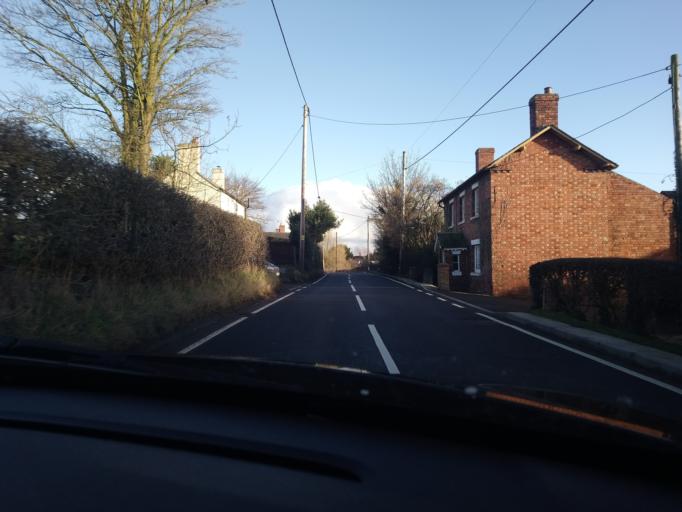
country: GB
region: England
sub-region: Shropshire
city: Ellesmere
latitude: 52.9083
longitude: -2.8336
